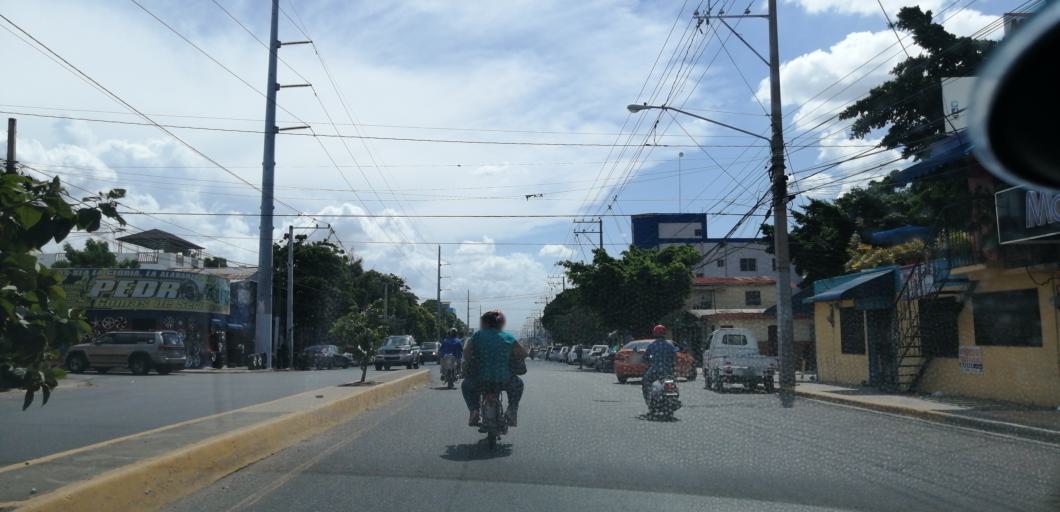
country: DO
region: Santiago
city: Santiago de los Caballeros
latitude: 19.4873
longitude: -70.7216
